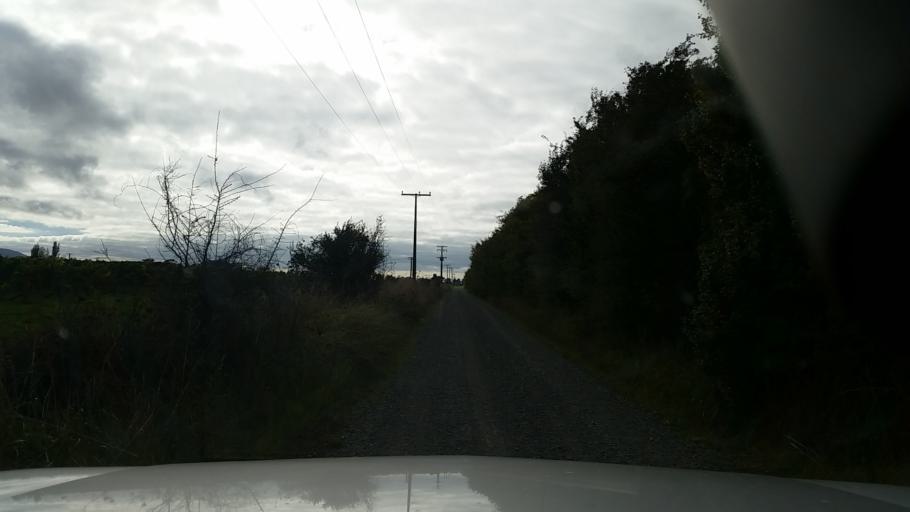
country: NZ
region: Marlborough
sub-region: Marlborough District
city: Blenheim
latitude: -41.4654
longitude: 173.9874
